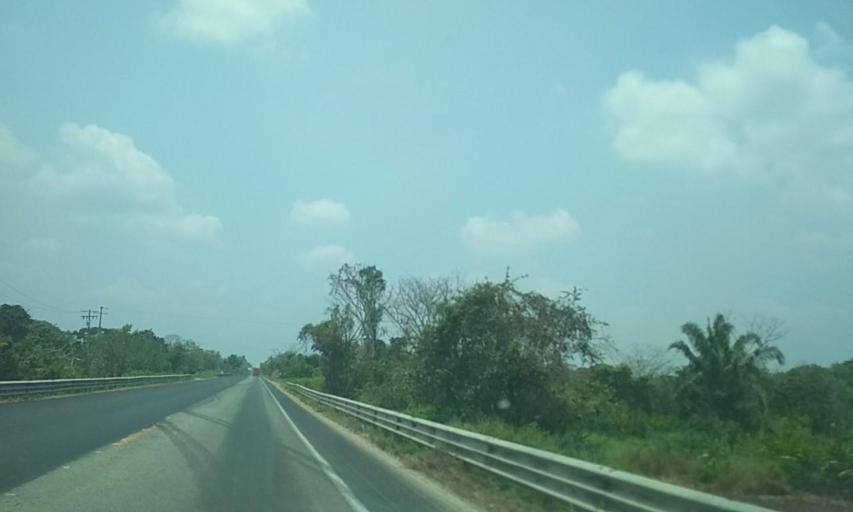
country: MX
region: Tabasco
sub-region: Huimanguillo
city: Francisco Rueda
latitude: 17.7191
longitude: -93.9517
